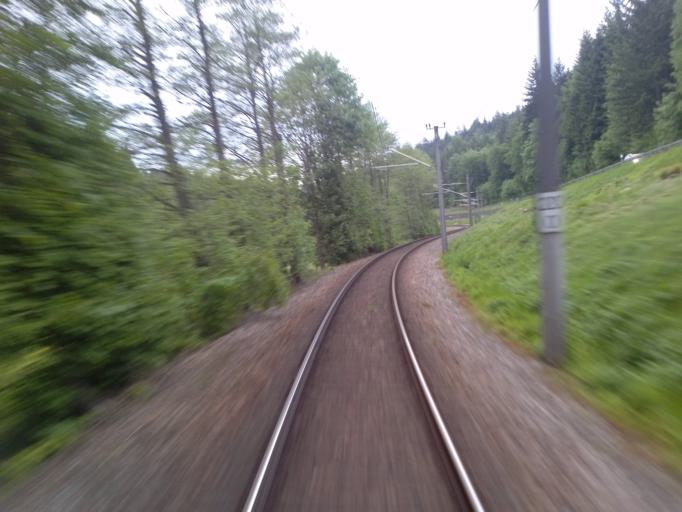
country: DE
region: Baden-Wuerttemberg
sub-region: Karlsruhe Region
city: Bad Herrenalb
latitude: 48.8497
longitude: 8.4385
